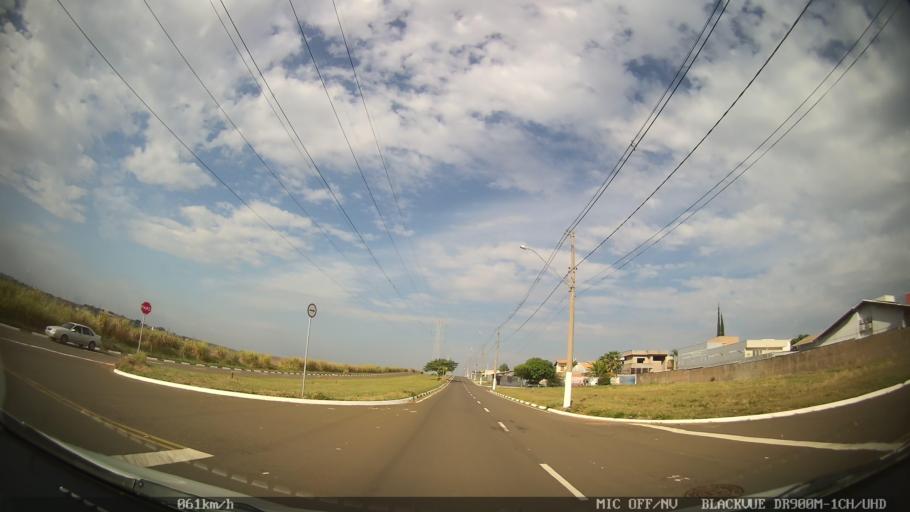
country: BR
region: Sao Paulo
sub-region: Paulinia
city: Paulinia
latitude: -22.7431
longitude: -47.1702
